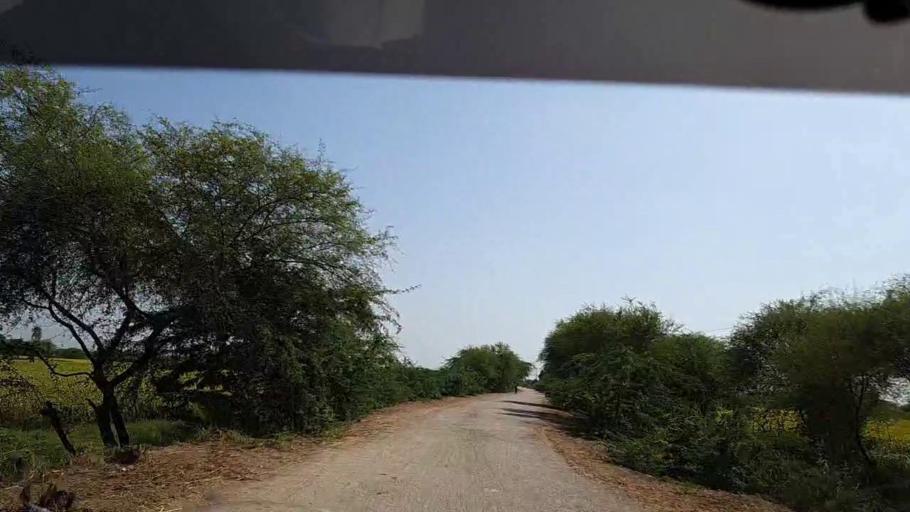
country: PK
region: Sindh
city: Badin
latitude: 24.6401
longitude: 68.7874
